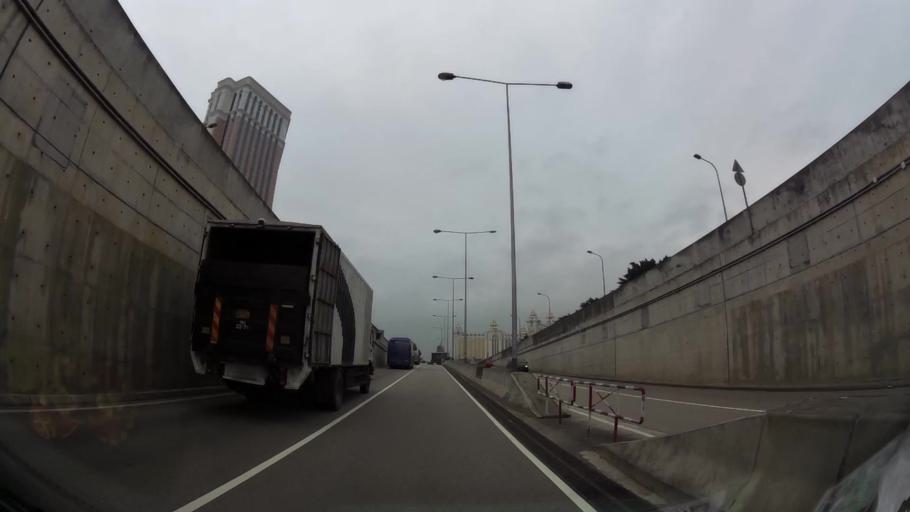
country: MO
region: Macau
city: Macau
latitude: 22.1507
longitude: 113.5625
